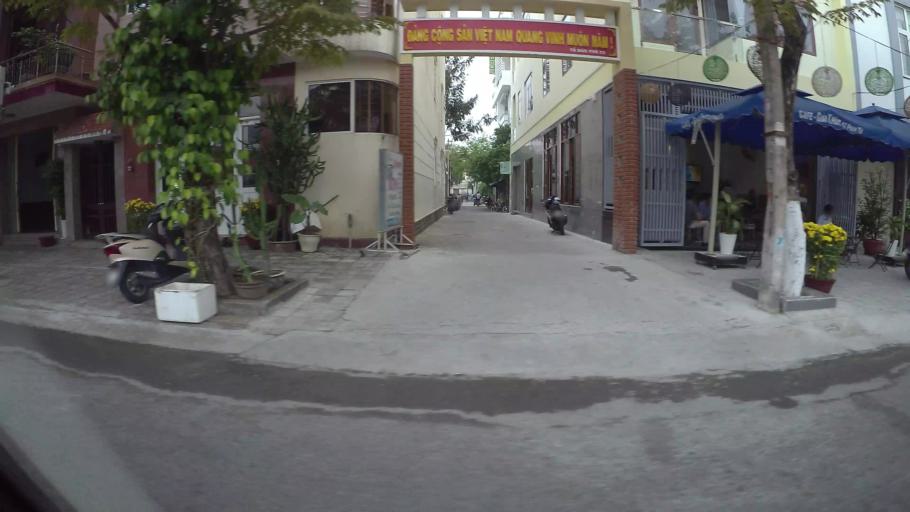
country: VN
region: Da Nang
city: Son Tra
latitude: 16.0462
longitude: 108.2449
